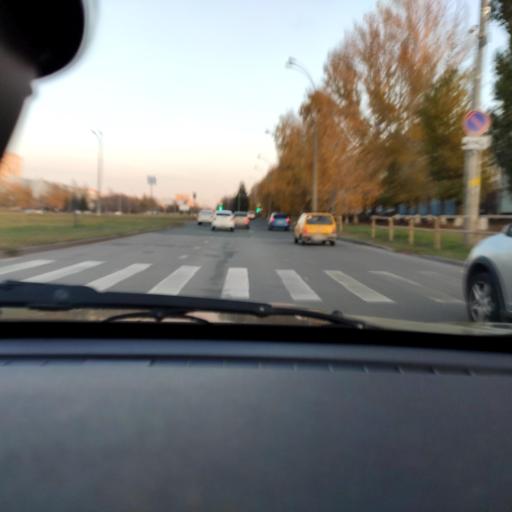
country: RU
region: Samara
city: Tol'yatti
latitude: 53.5285
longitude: 49.2820
